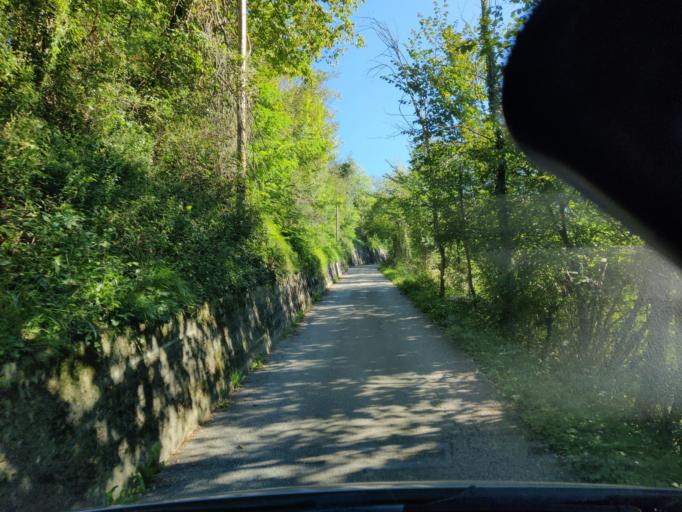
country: IT
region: Veneto
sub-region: Provincia di Belluno
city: Ponte nelle Alpi-Polpet
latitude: 46.1790
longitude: 12.2708
